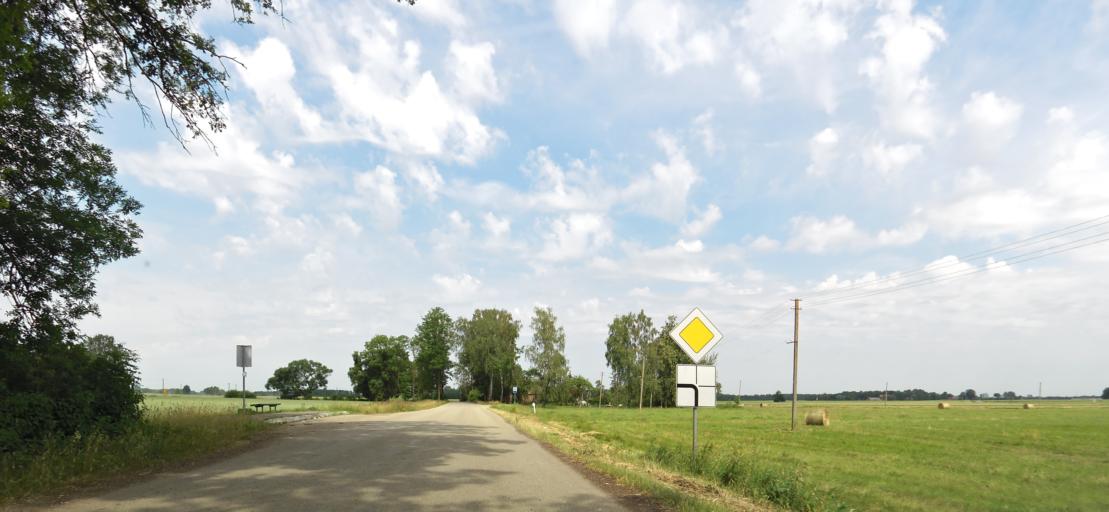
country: LT
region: Panevezys
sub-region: Birzai
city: Birzai
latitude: 56.2740
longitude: 24.6008
